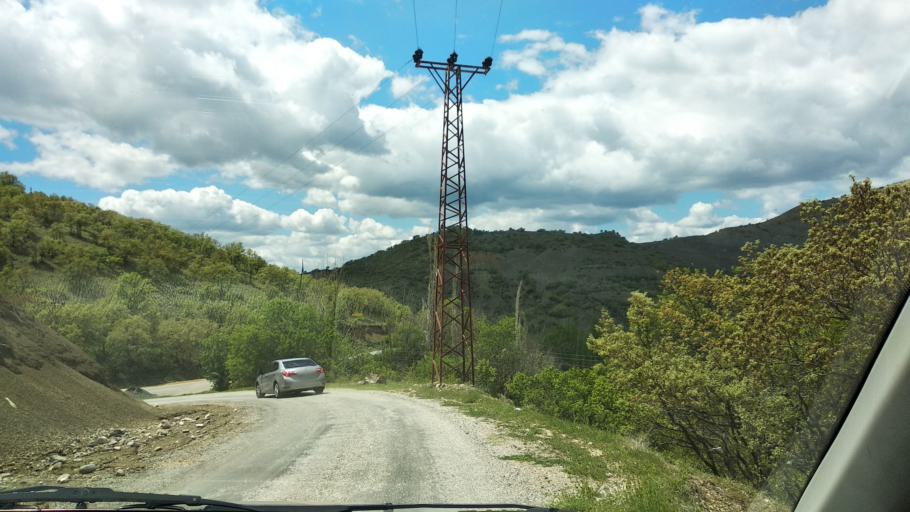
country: TR
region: Bolu
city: Seben
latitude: 40.4276
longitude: 31.5937
